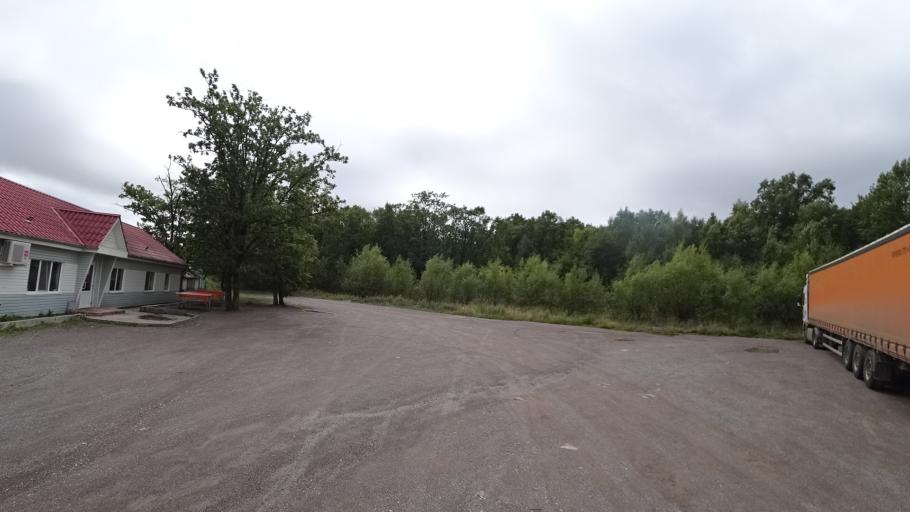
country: RU
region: Primorskiy
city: Monastyrishche
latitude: 44.1639
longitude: 132.4394
